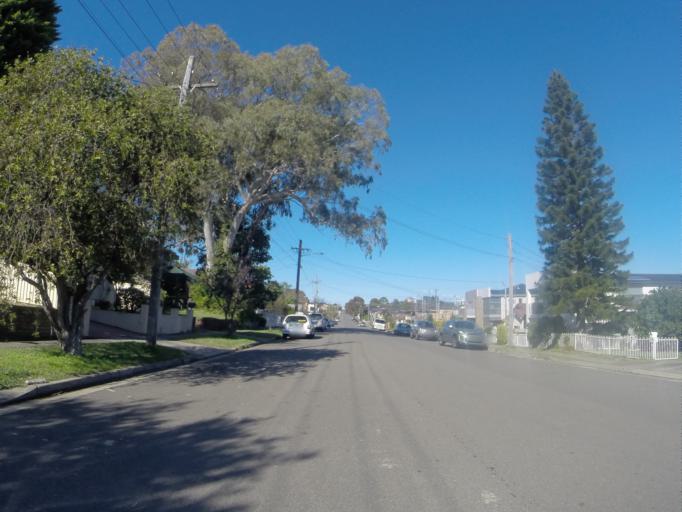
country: AU
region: New South Wales
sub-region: Hurstville
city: Earlwood
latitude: -33.9537
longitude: 151.0904
